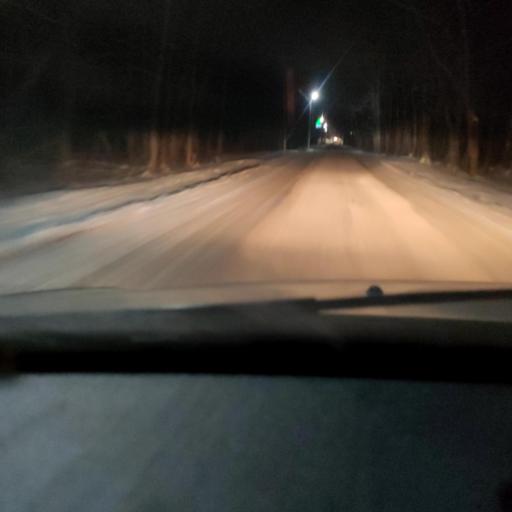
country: RU
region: Bashkortostan
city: Ufa
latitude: 54.7033
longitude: 55.9254
